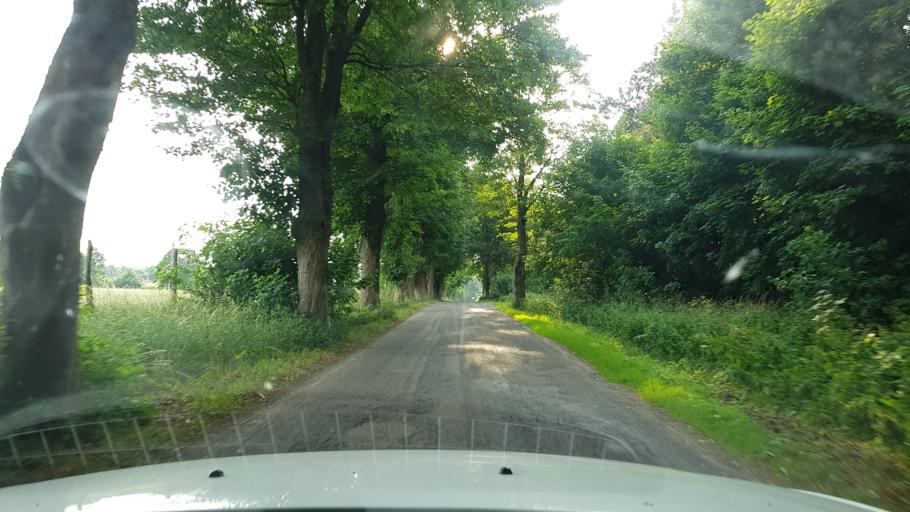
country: PL
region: West Pomeranian Voivodeship
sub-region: Powiat swidwinski
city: Swidwin
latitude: 53.8026
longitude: 15.8339
